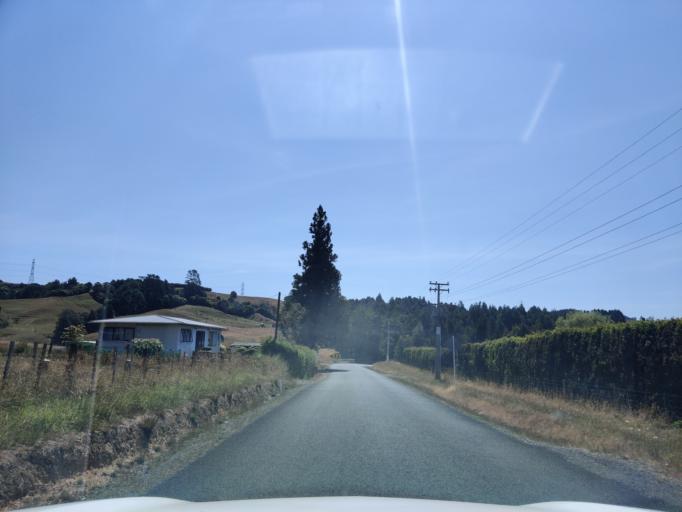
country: NZ
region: Auckland
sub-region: Auckland
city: Red Hill
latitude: -37.0653
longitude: 175.0845
